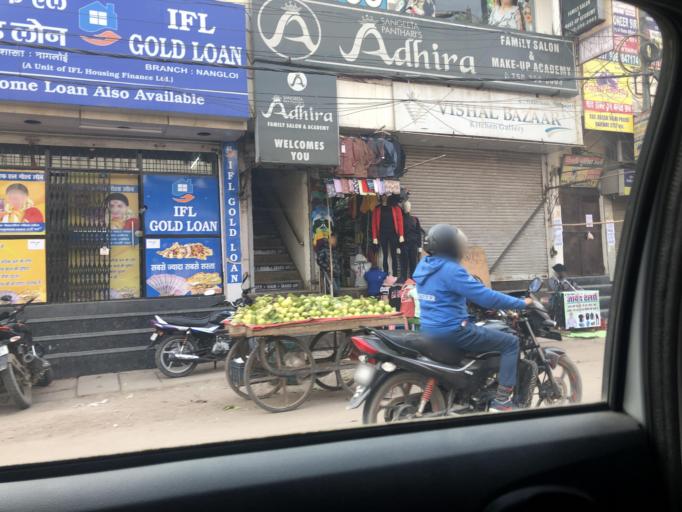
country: IN
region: NCT
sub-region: West Delhi
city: Nangloi Jat
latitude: 28.6819
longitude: 77.0687
